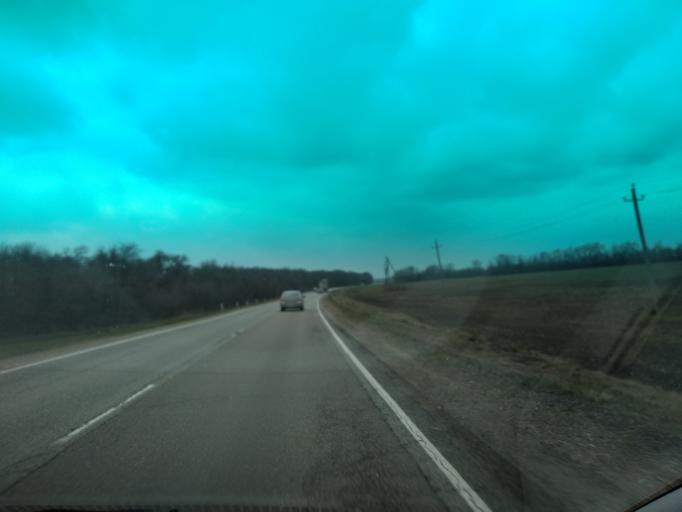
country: RU
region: Krasnodarskiy
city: Novomalorossiyskaya
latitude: 45.7283
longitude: 39.9039
